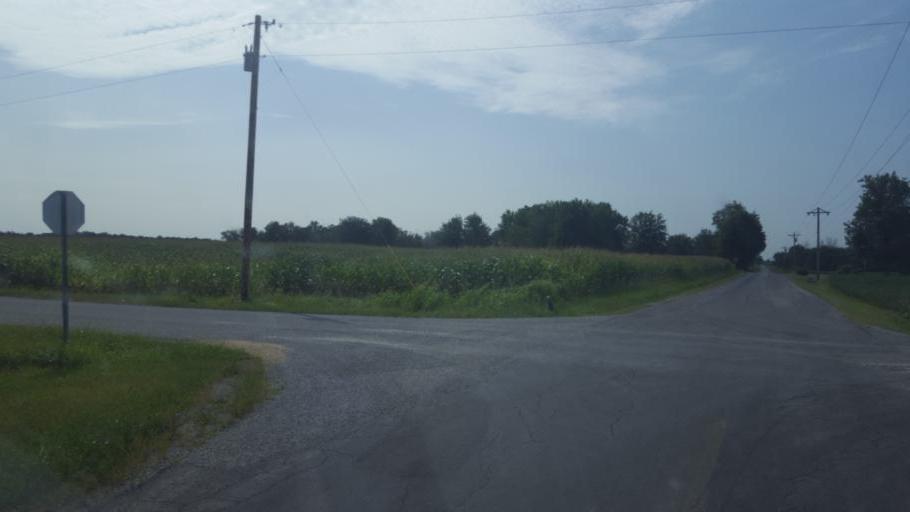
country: US
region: Ohio
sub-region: Morrow County
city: Cardington
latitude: 40.5284
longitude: -82.9957
